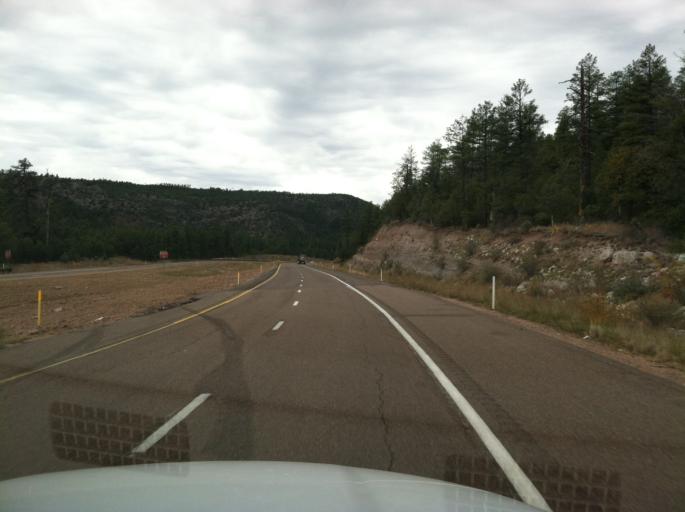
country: US
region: Arizona
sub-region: Gila County
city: Star Valley
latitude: 34.3133
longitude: -111.0393
